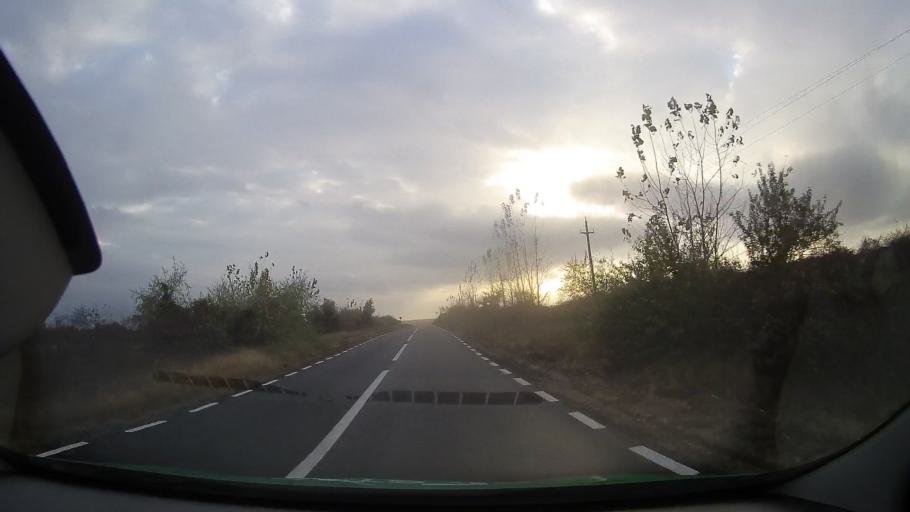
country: RO
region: Constanta
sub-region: Comuna Adamclisi
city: Adamclisi
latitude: 44.0667
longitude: 27.9750
